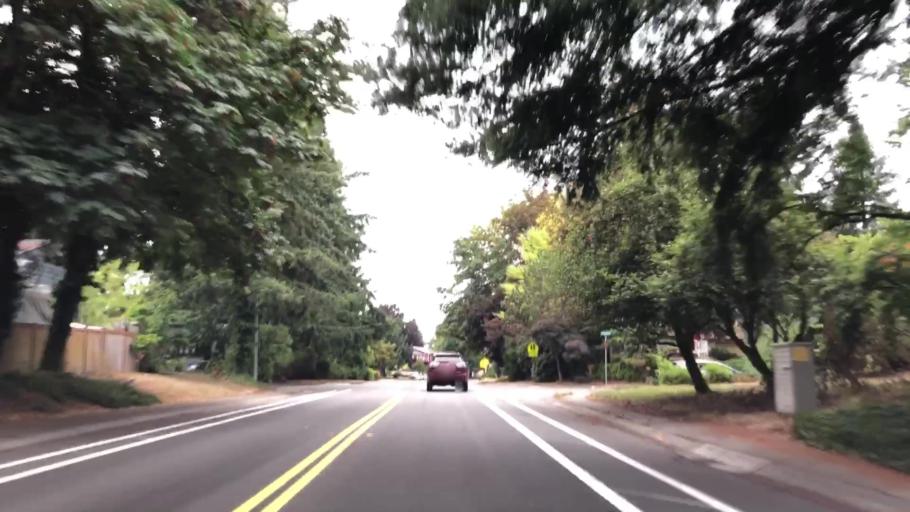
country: US
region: Washington
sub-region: King County
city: Kingsgate
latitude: 47.7304
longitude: -122.1656
